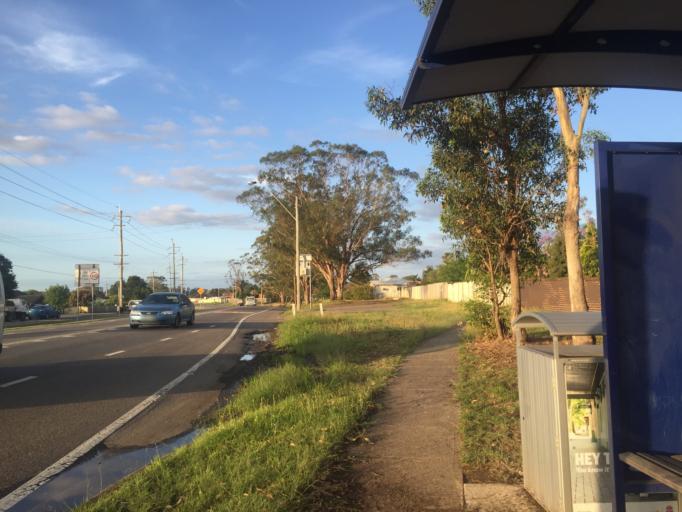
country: AU
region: New South Wales
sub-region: Blacktown
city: Blacktown
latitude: -33.7877
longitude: 150.9202
